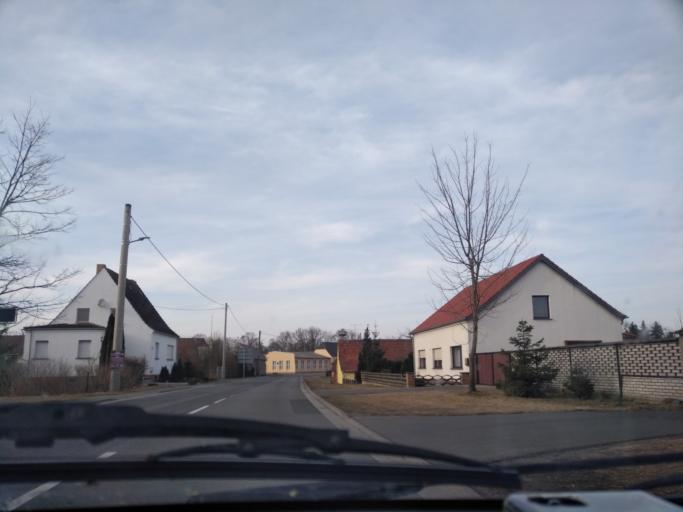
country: DE
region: Saxony-Anhalt
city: Holzdorf
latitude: 51.7960
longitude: 13.1790
